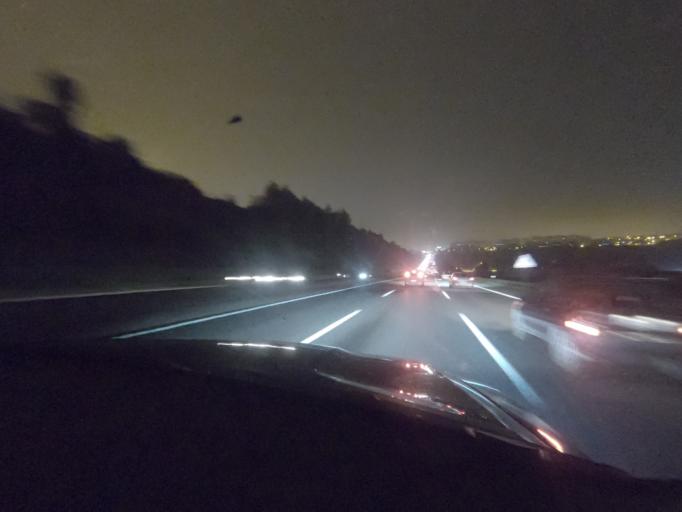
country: PT
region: Lisbon
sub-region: Loures
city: Bobadela
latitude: 38.8064
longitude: -9.1049
